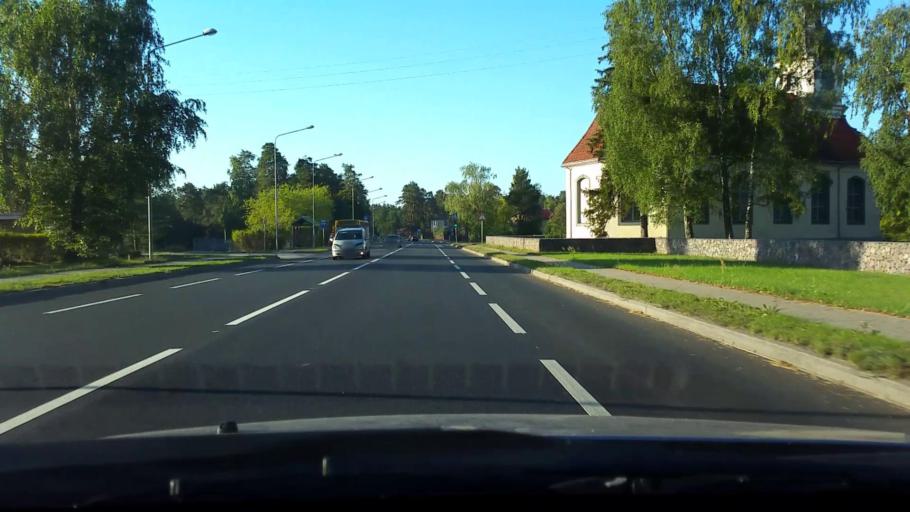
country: LV
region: Adazi
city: Adazi
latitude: 57.0449
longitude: 24.3160
